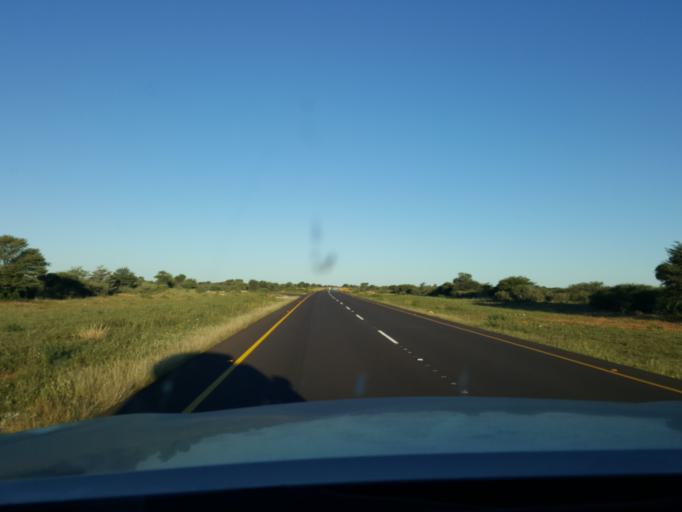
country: BW
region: Southern
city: Sekoma
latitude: -24.4467
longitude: 23.7643
